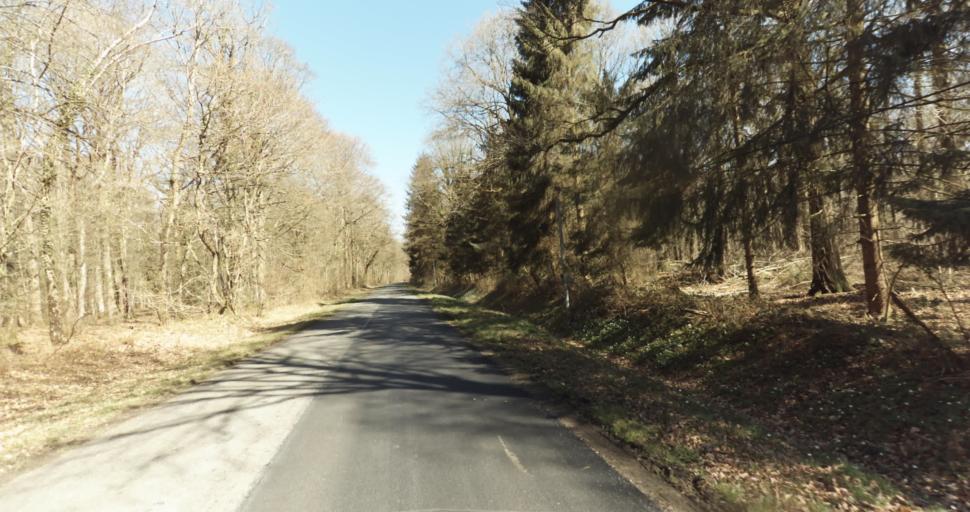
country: FR
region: Lower Normandy
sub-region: Departement de l'Orne
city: Trun
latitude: 48.9298
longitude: 0.0691
